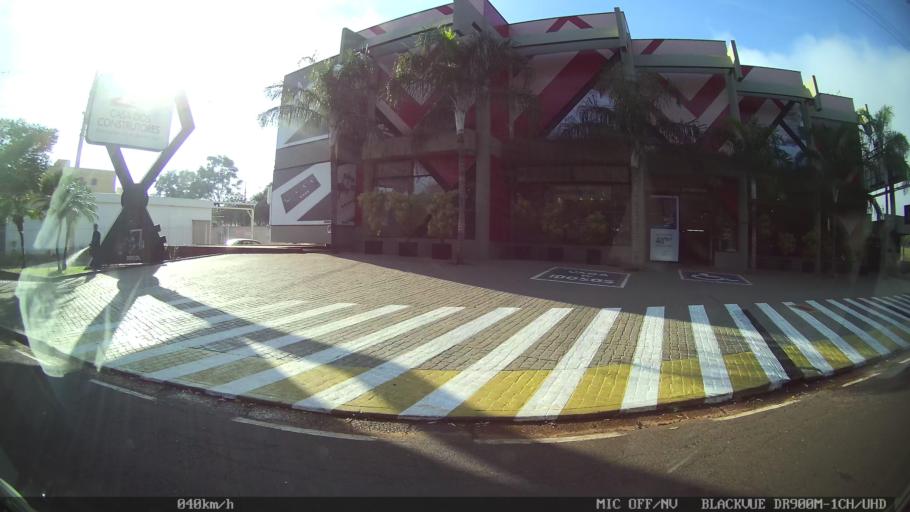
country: BR
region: Sao Paulo
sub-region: Sao Jose Do Rio Preto
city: Sao Jose do Rio Preto
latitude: -20.8251
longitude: -49.3657
